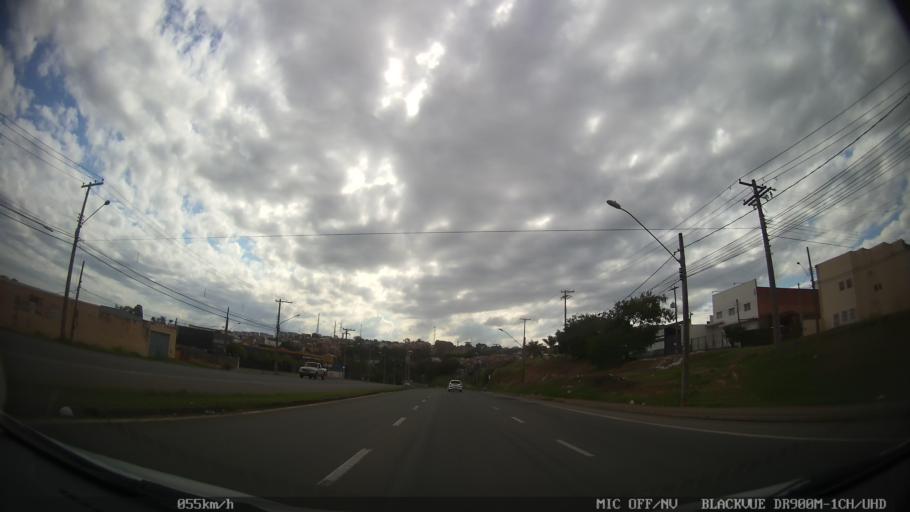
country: BR
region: Sao Paulo
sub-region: Limeira
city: Limeira
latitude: -22.5489
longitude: -47.3844
